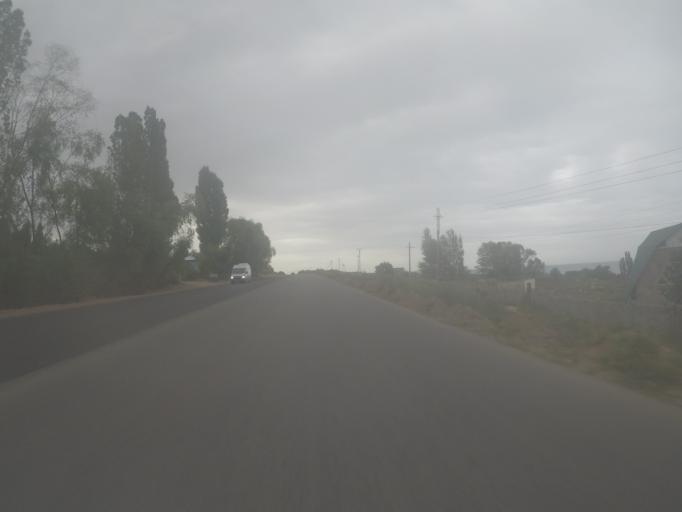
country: KG
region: Ysyk-Koel
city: Cholpon-Ata
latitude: 42.6788
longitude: 77.3182
